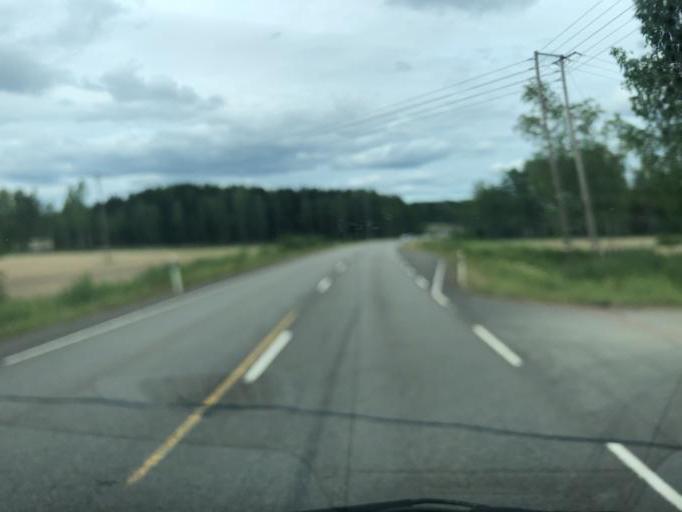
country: FI
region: Kymenlaakso
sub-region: Kouvola
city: Kouvola
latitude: 60.9444
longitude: 26.8328
